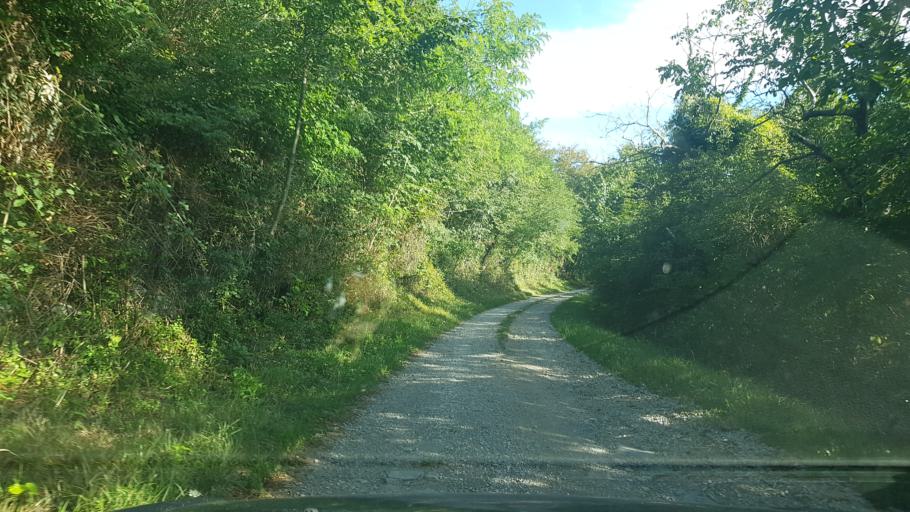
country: SI
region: Kanal
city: Deskle
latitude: 46.0189
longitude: 13.6191
